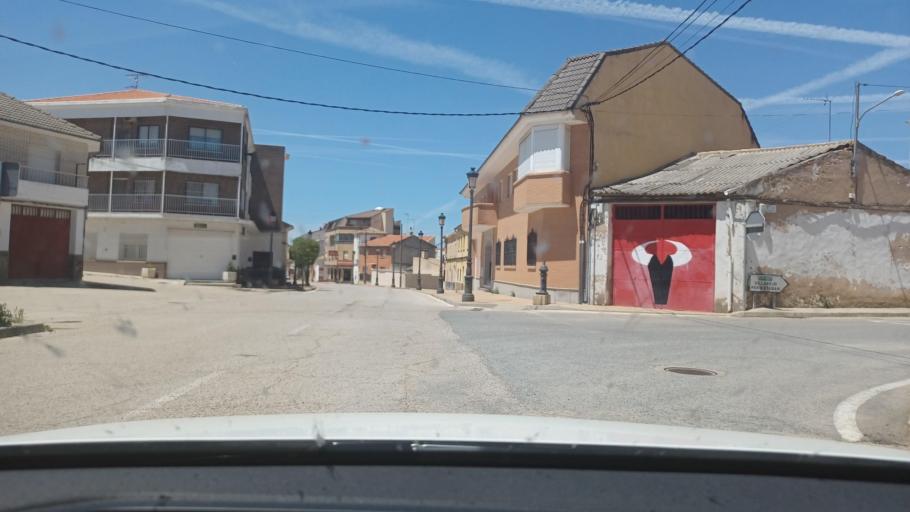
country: ES
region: Castille-La Mancha
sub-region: Provincia de Cuenca
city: Villares del Saz
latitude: 39.8389
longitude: -2.5029
